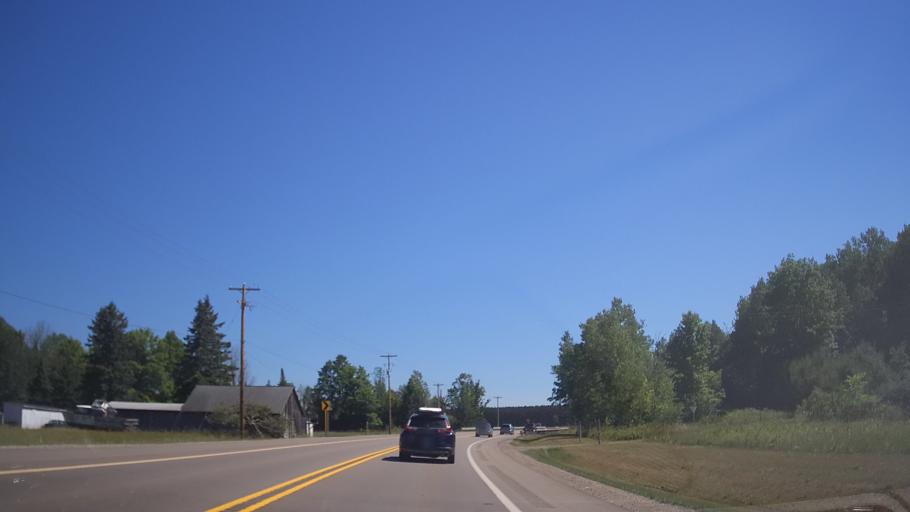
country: US
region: Michigan
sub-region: Mackinac County
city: Saint Ignace
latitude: 45.6187
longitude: -84.7802
